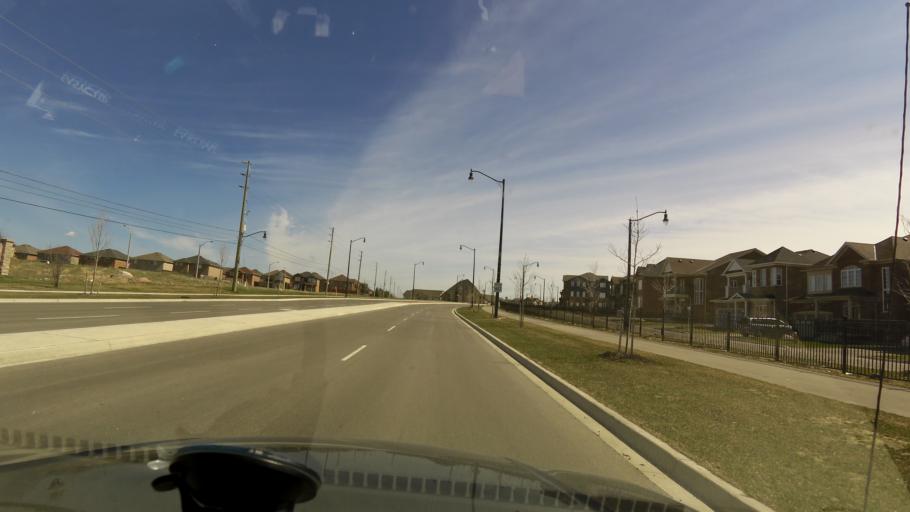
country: CA
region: Ontario
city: Brampton
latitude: 43.6837
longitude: -79.8290
